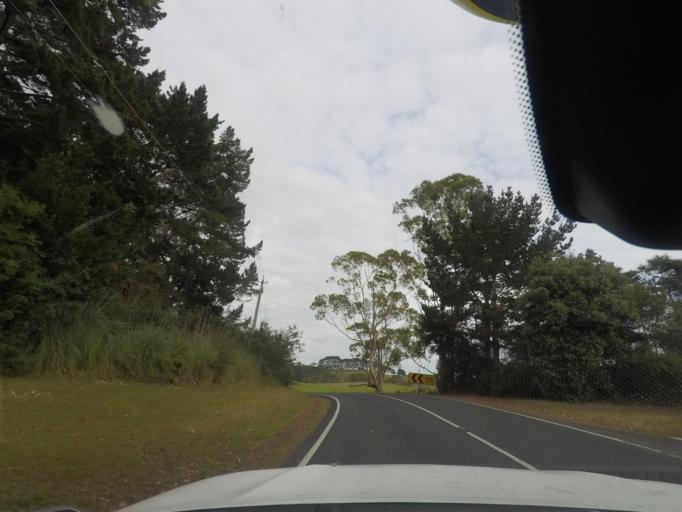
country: NZ
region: Auckland
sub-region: Auckland
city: Parakai
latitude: -36.5251
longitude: 174.2887
